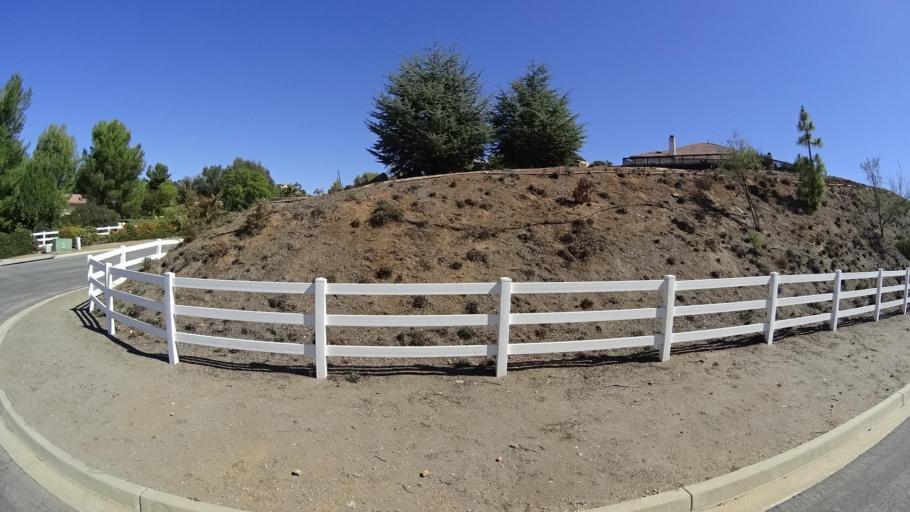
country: US
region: California
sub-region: San Diego County
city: Alpine
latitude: 32.8085
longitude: -116.7763
